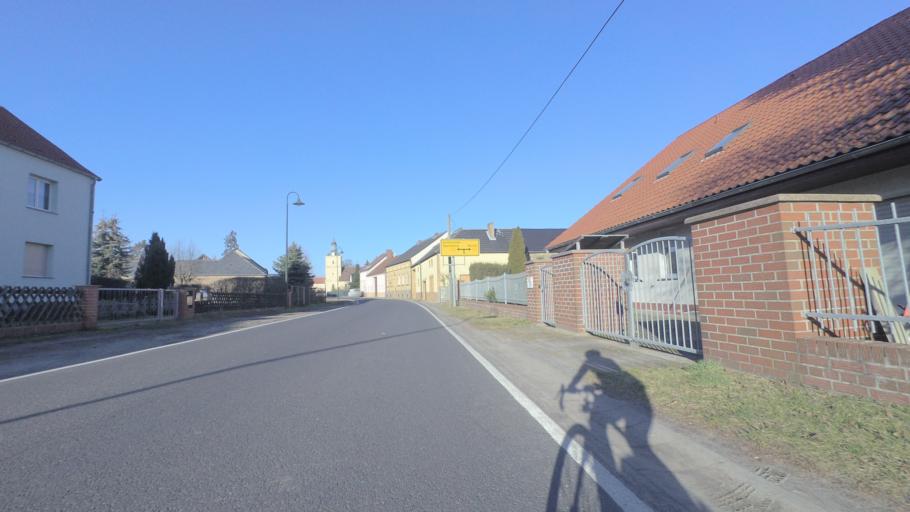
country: DE
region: Brandenburg
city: Sperenberg
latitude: 52.0448
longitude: 13.3229
